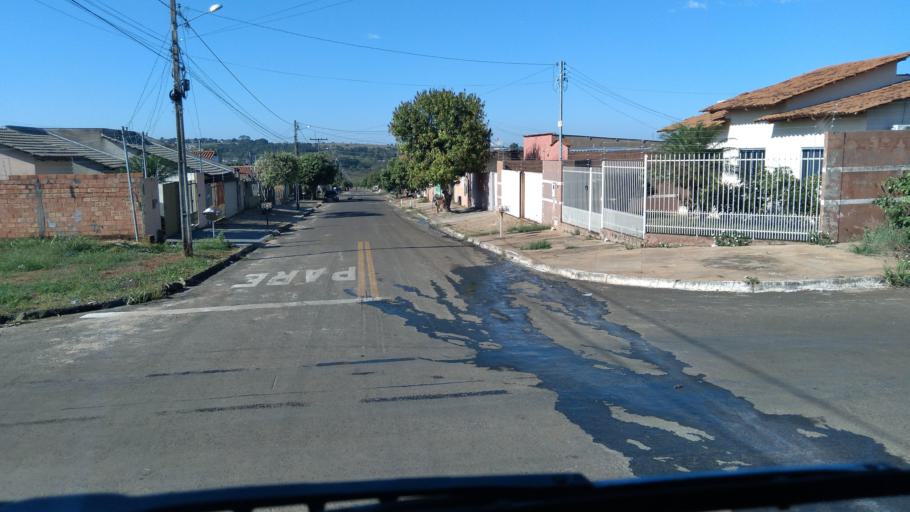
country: BR
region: Goias
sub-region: Mineiros
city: Mineiros
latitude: -17.5747
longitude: -52.5718
